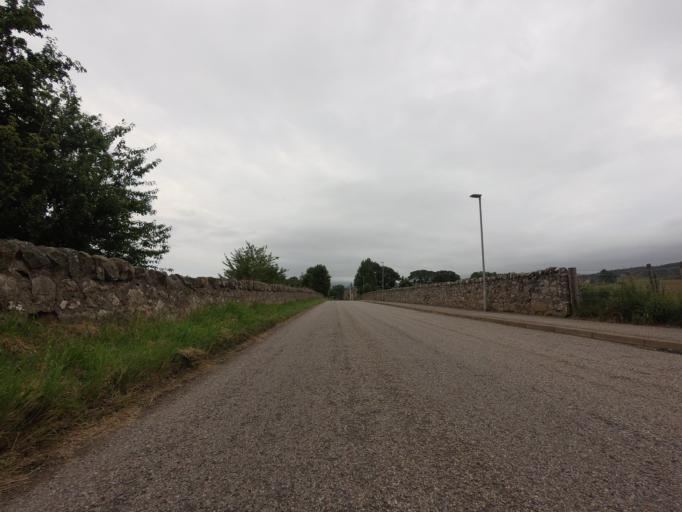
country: GB
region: Scotland
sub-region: Highland
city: Alness
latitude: 57.8846
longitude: -4.3661
